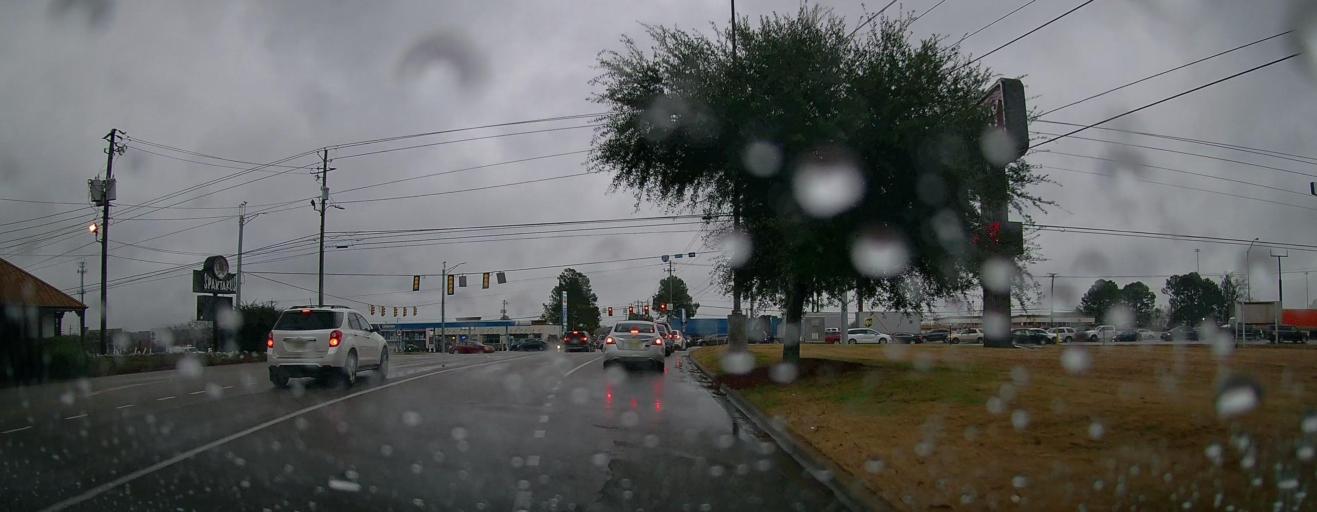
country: US
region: Alabama
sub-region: Montgomery County
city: Montgomery
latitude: 32.3661
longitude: -86.2124
